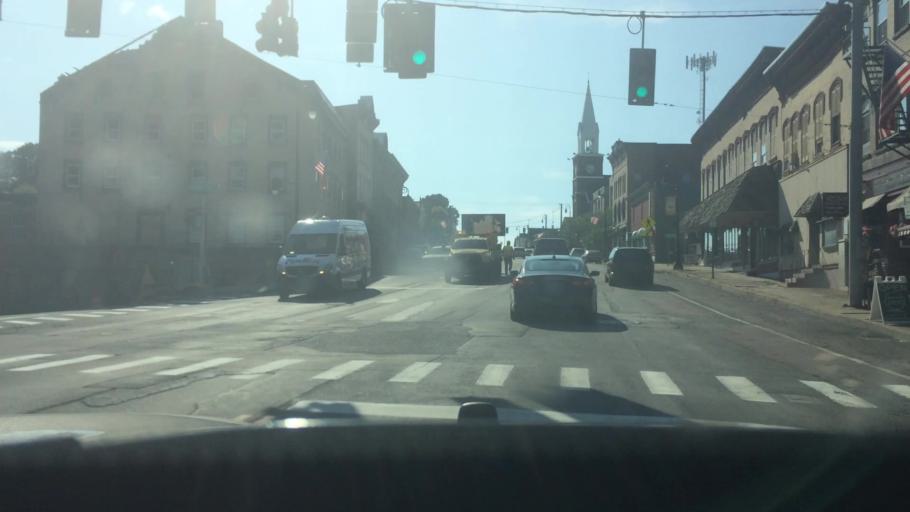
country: US
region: New York
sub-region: Franklin County
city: Malone
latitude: 44.8488
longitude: -74.2935
